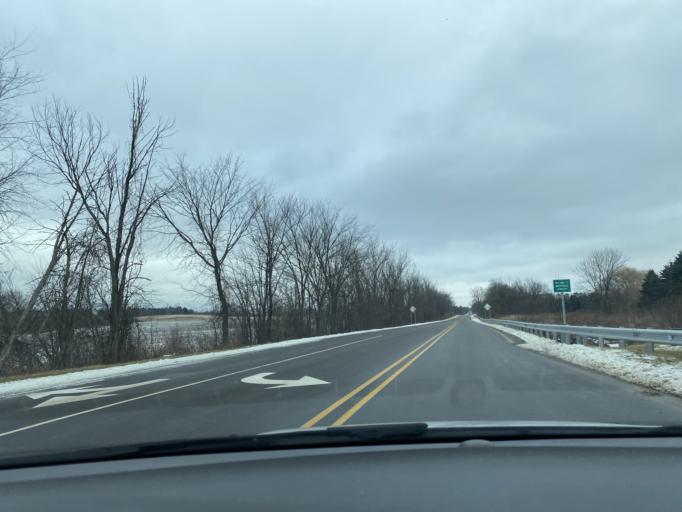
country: US
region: Michigan
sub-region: Lapeer County
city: Lapeer
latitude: 43.0719
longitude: -83.3436
